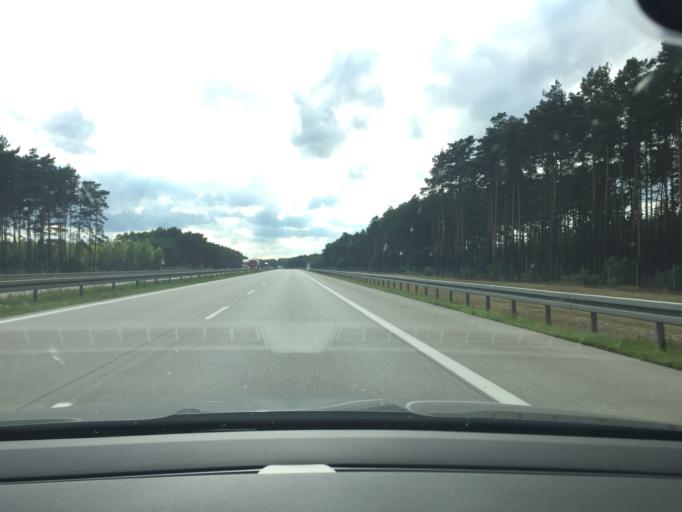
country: PL
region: Lubusz
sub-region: Powiat slubicki
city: Rzepin
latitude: 52.3354
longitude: 14.7673
